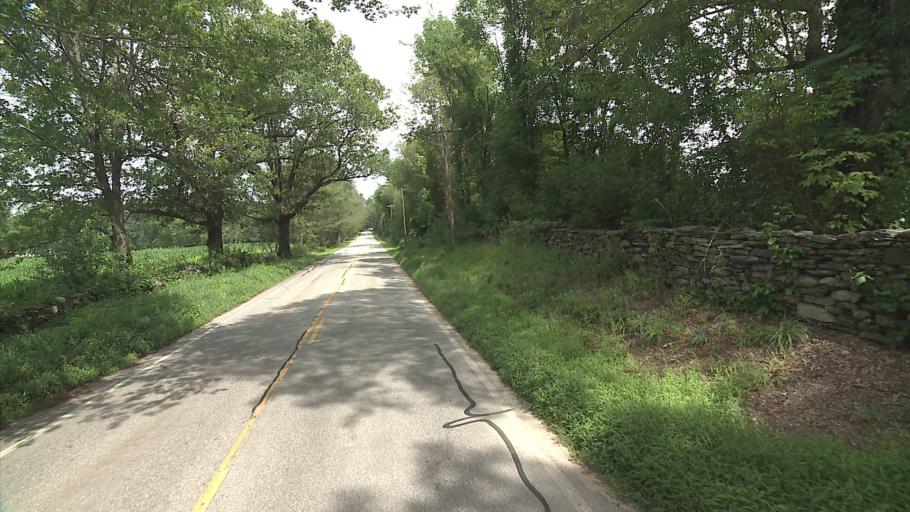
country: US
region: Connecticut
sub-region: Windham County
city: Thompson
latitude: 41.9412
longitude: -71.8656
